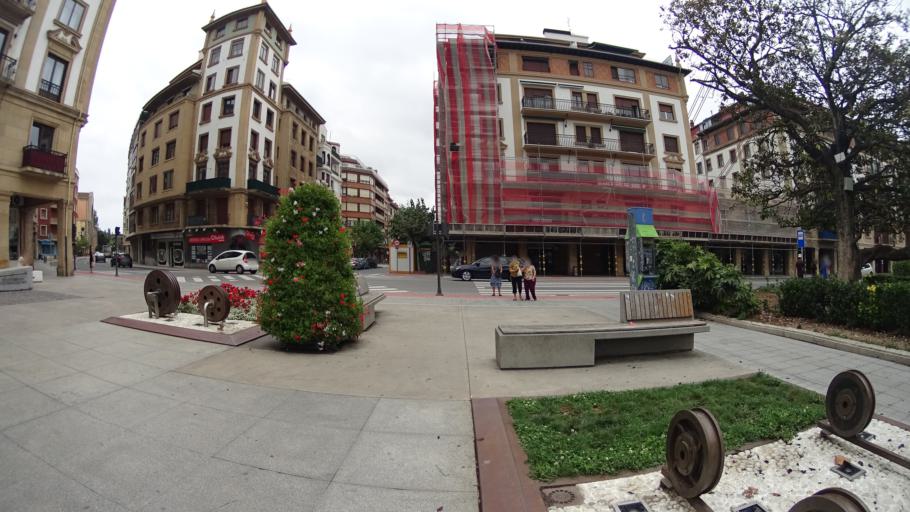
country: ES
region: Basque Country
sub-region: Bizkaia
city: Portugalete
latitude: 43.3241
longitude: -3.0161
